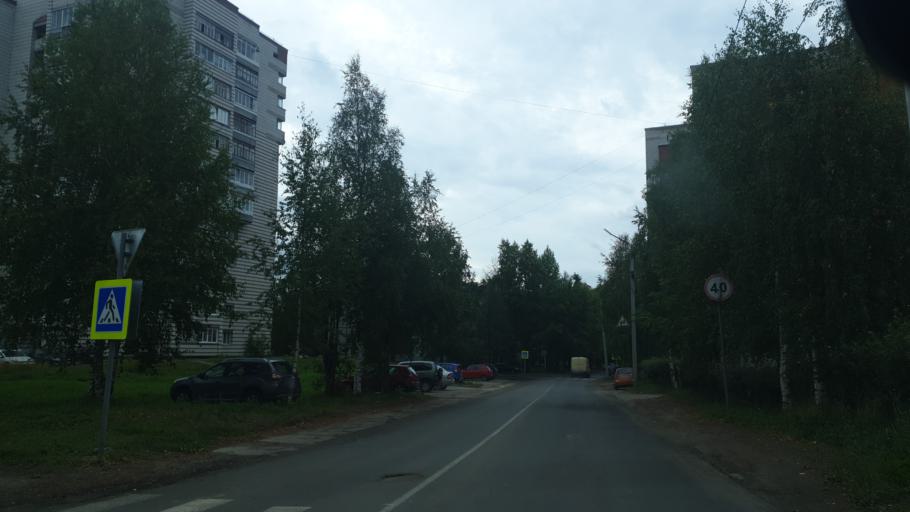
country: RU
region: Komi Republic
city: Ezhva
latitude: 61.7951
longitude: 50.7406
